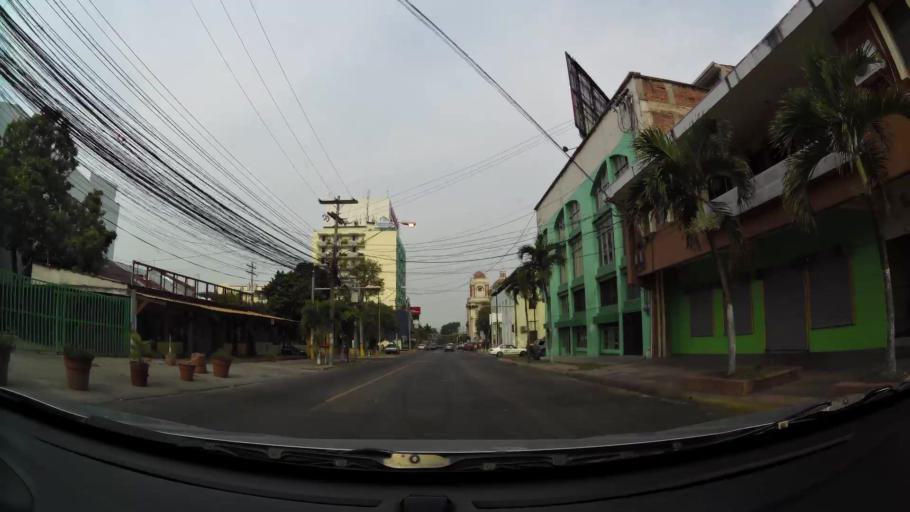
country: HN
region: Cortes
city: San Pedro Sula
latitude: 15.5059
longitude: -88.0262
